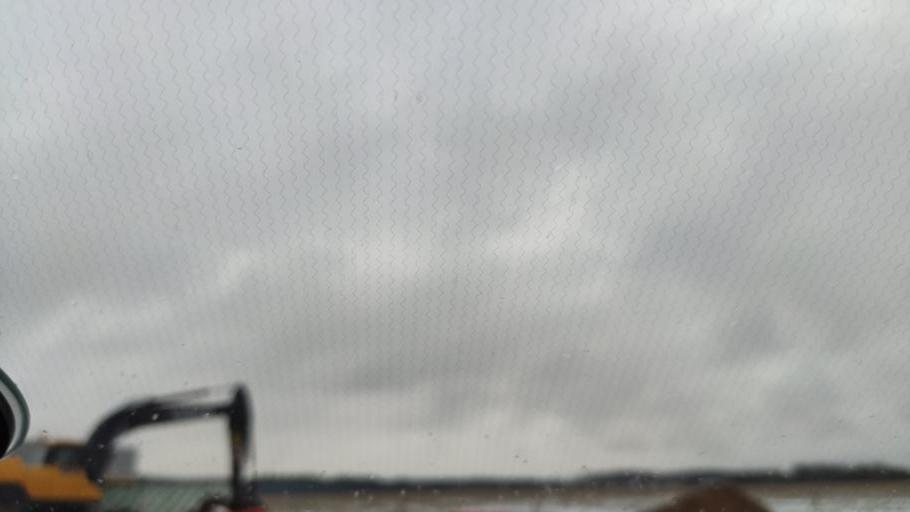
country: RU
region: Moskovskaya
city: Vatutinki
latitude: 55.4627
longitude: 37.3769
